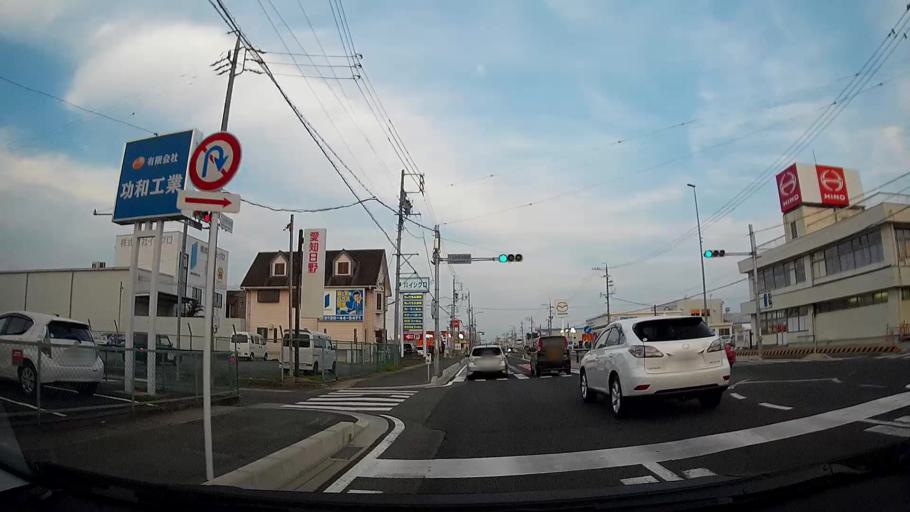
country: JP
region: Aichi
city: Kozakai-cho
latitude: 34.7902
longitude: 137.3736
